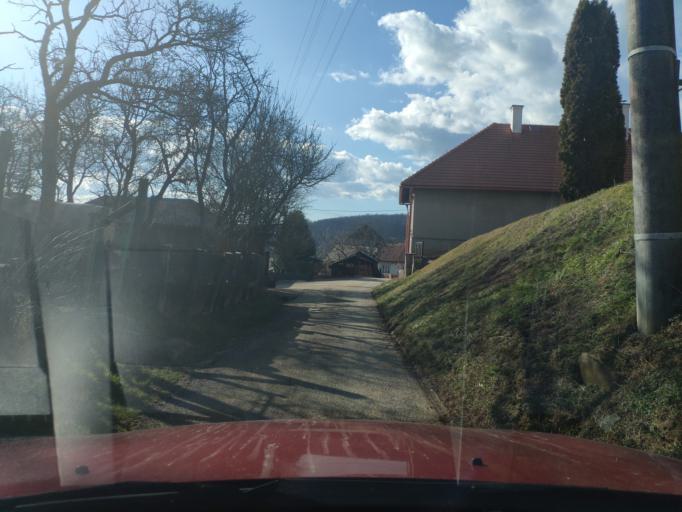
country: HU
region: Borsod-Abauj-Zemplen
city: Putnok
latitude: 48.4971
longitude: 20.3773
